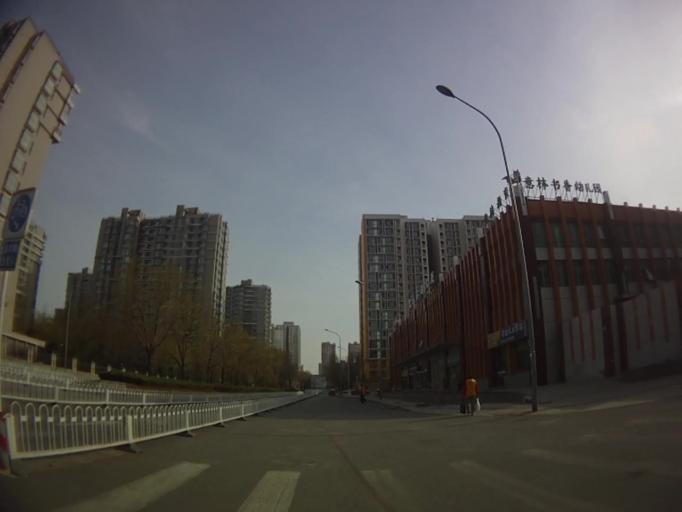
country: CN
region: Beijing
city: Longtan
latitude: 39.8959
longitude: 116.4441
